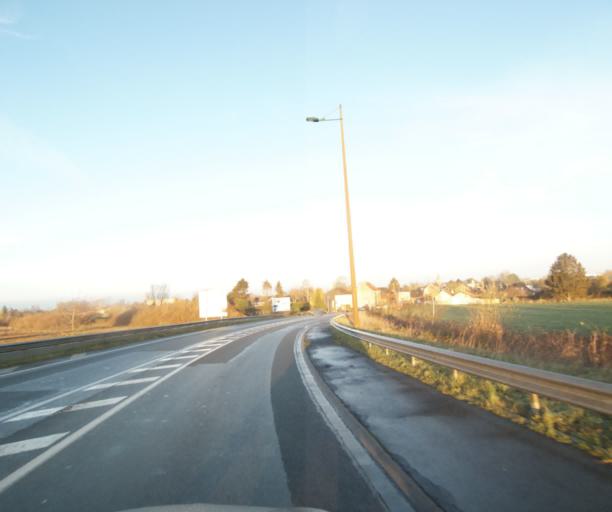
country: FR
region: Nord-Pas-de-Calais
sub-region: Departement du Nord
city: Onnaing
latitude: 50.3809
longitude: 3.6063
